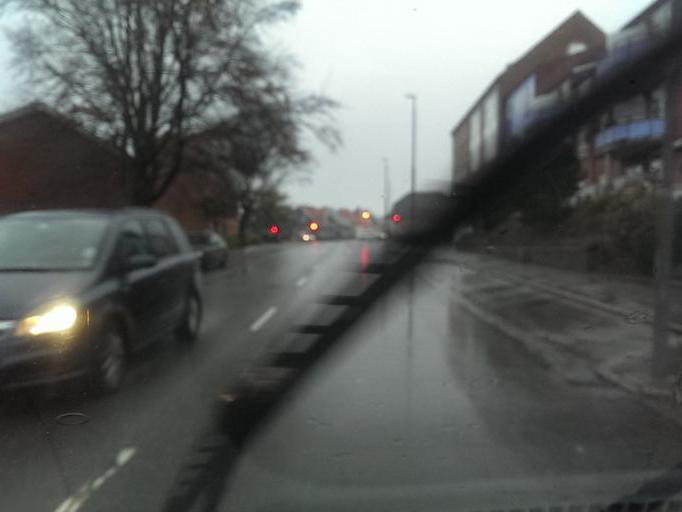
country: DK
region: South Denmark
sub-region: Esbjerg Kommune
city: Esbjerg
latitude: 55.4703
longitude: 8.4661
